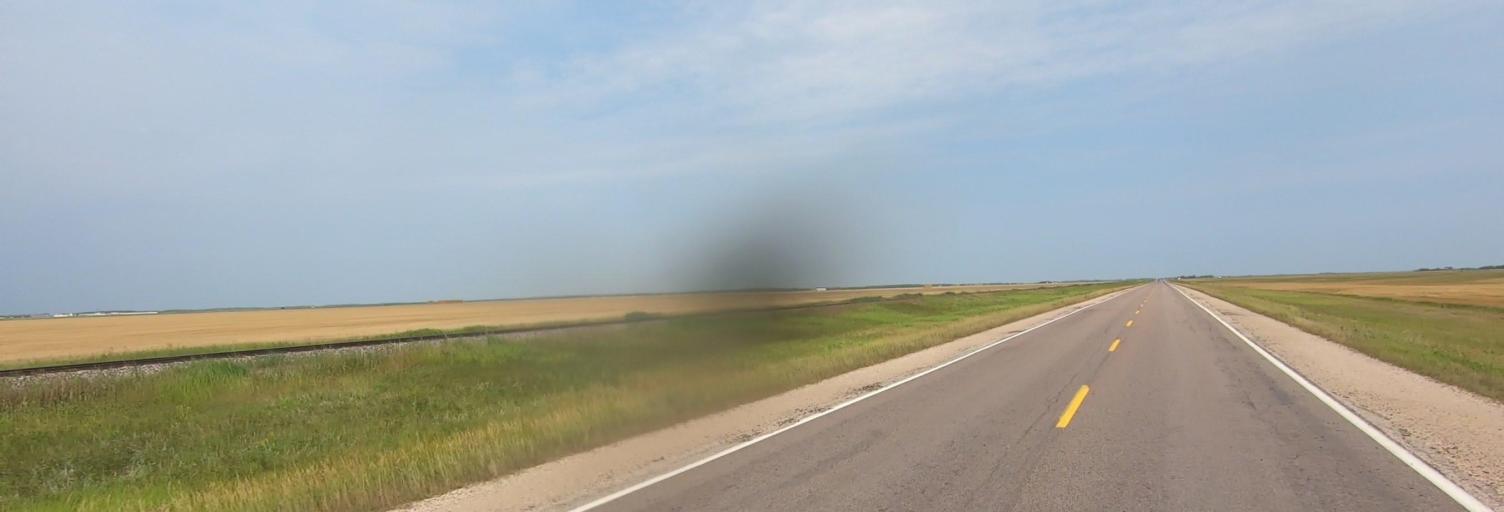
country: CA
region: Manitoba
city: Headingley
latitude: 49.6245
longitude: -97.3137
